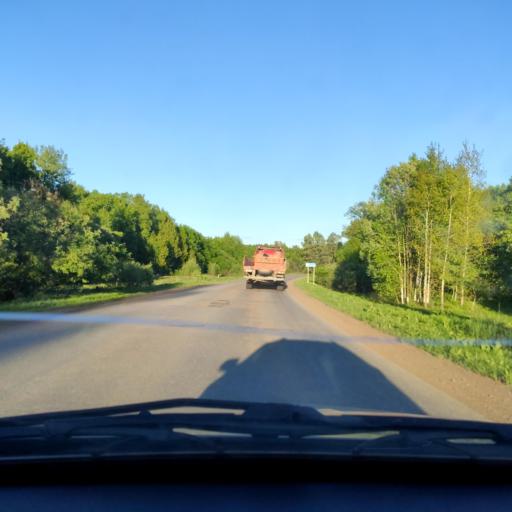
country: RU
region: Bashkortostan
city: Blagoveshchensk
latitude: 55.0318
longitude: 56.1036
